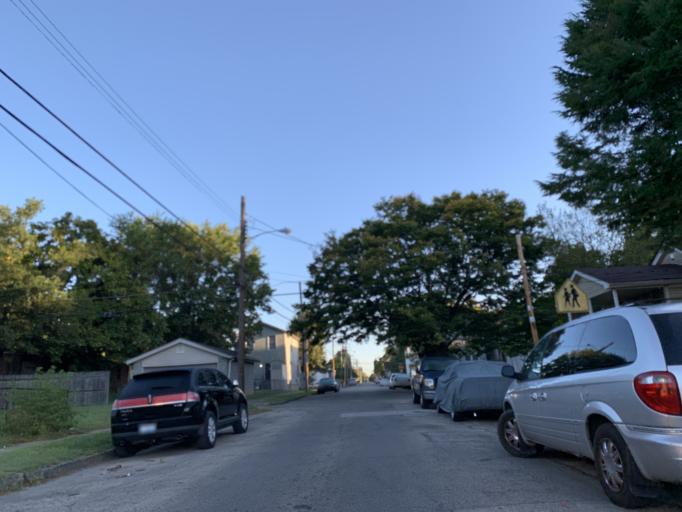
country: US
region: Kentucky
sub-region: Jefferson County
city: Louisville
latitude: 38.2378
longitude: -85.7808
